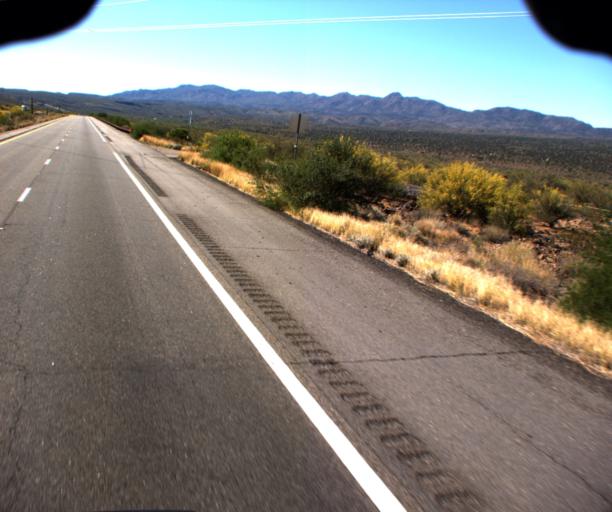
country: US
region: Arizona
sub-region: Yavapai County
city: Bagdad
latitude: 34.5291
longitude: -113.4296
